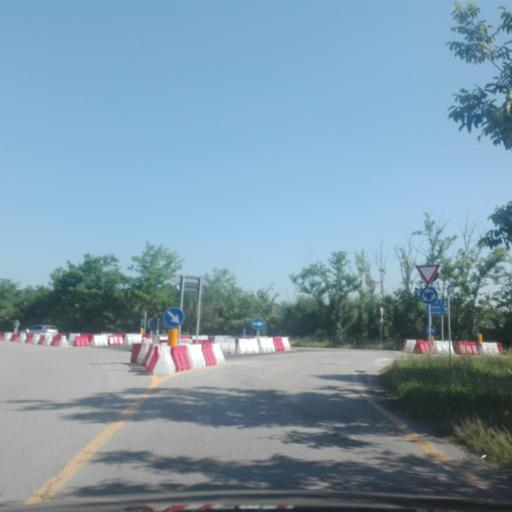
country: IT
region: Veneto
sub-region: Provincia di Rovigo
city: Gavello
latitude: 45.0339
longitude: 11.9193
